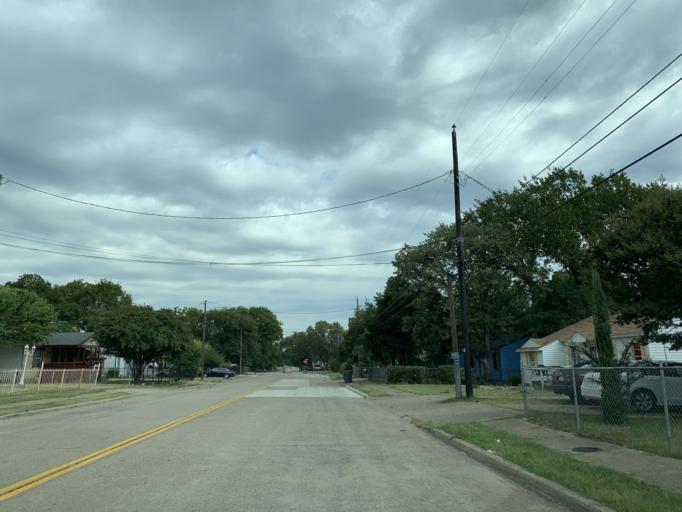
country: US
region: Texas
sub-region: Dallas County
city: Duncanville
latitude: 32.6679
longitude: -96.8290
